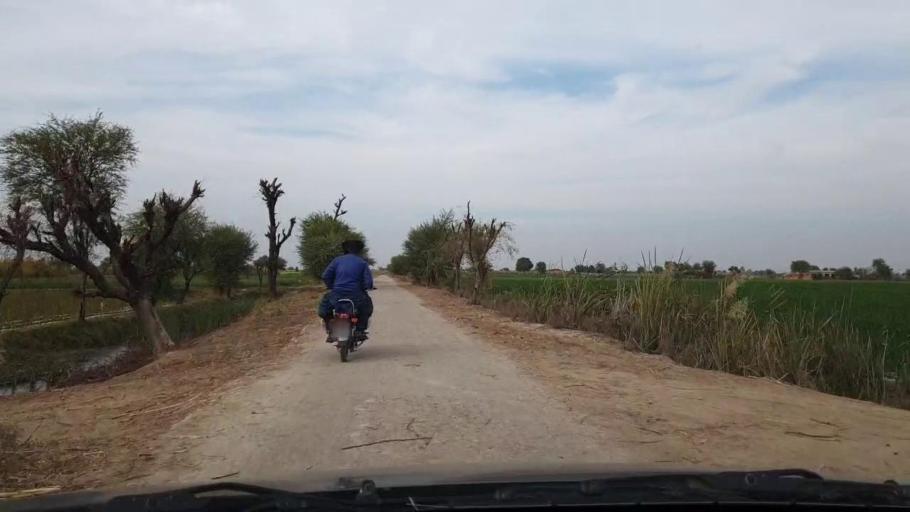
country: PK
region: Sindh
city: Khadro
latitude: 26.1656
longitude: 68.7300
